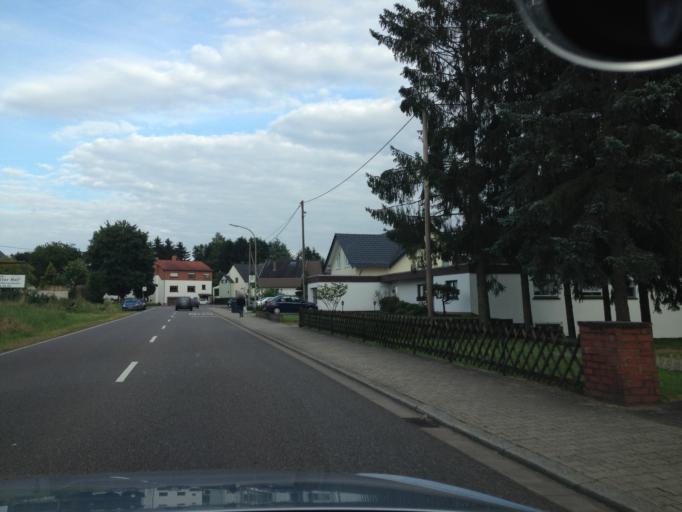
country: DE
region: Saarland
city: Illingen
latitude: 49.3775
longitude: 7.0887
